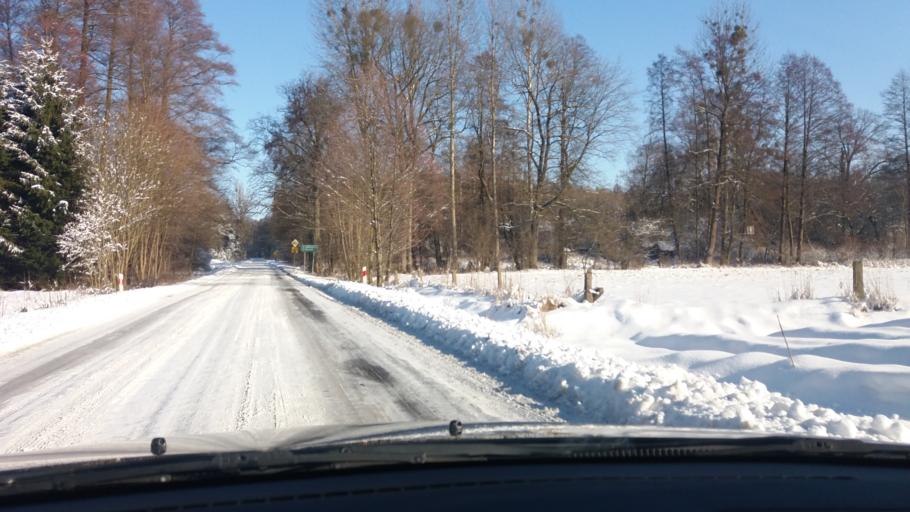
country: PL
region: Warmian-Masurian Voivodeship
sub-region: Powiat nidzicki
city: Nidzica
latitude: 53.3512
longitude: 20.6150
